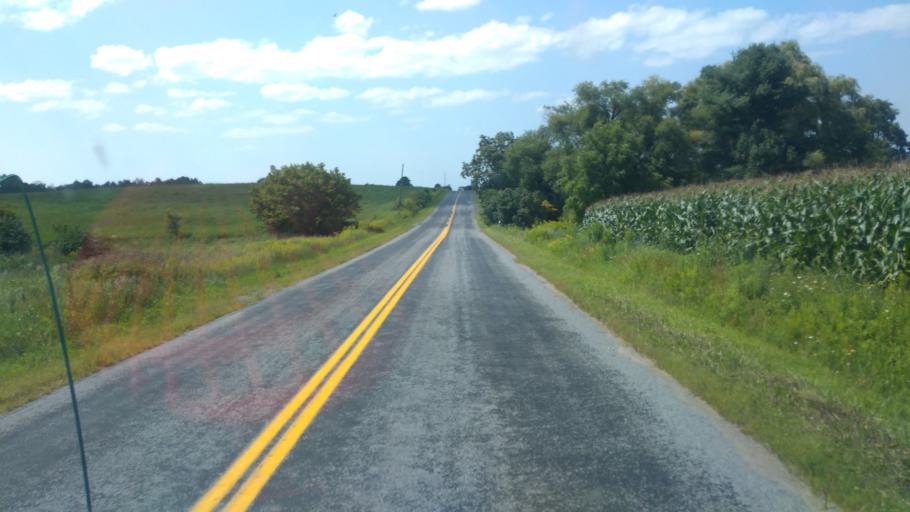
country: US
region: New York
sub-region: Steuben County
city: Canisteo
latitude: 42.3538
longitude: -77.5581
